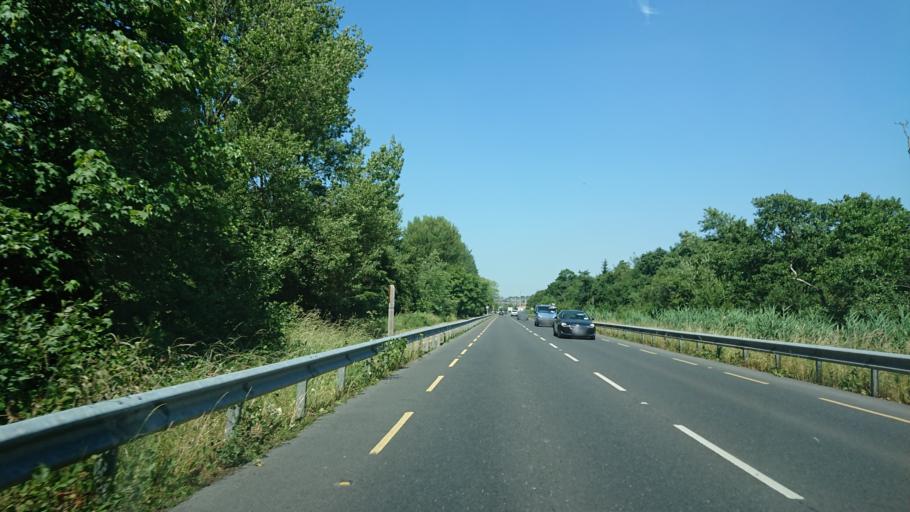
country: IE
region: Munster
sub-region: Waterford
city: Waterford
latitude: 52.2418
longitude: -7.1209
